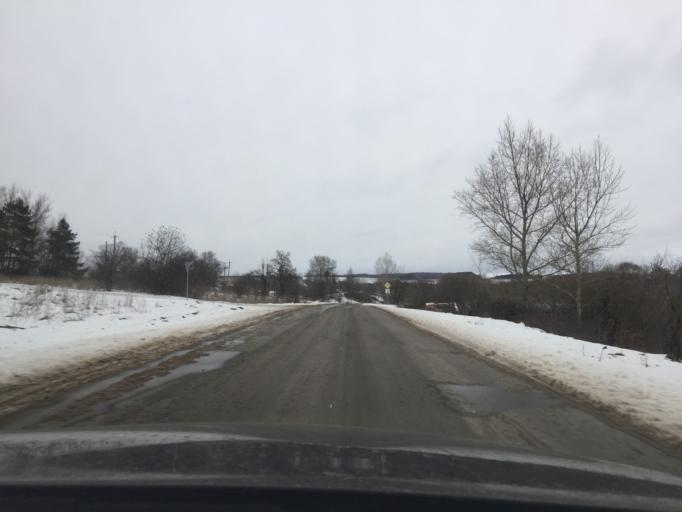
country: RU
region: Tula
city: Shchekino
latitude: 53.8304
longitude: 37.5605
